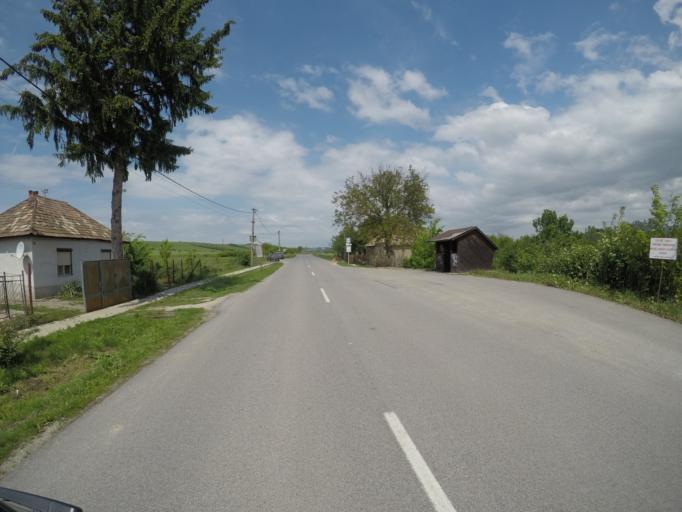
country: SK
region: Nitriansky
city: Zeliezovce
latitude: 47.9757
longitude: 18.7529
